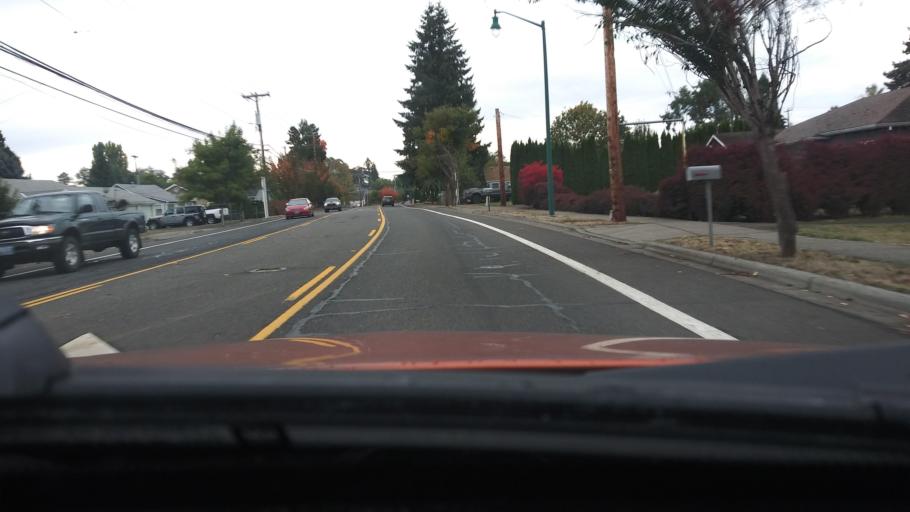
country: US
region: Oregon
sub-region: Washington County
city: Forest Grove
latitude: 45.5318
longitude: -123.1078
